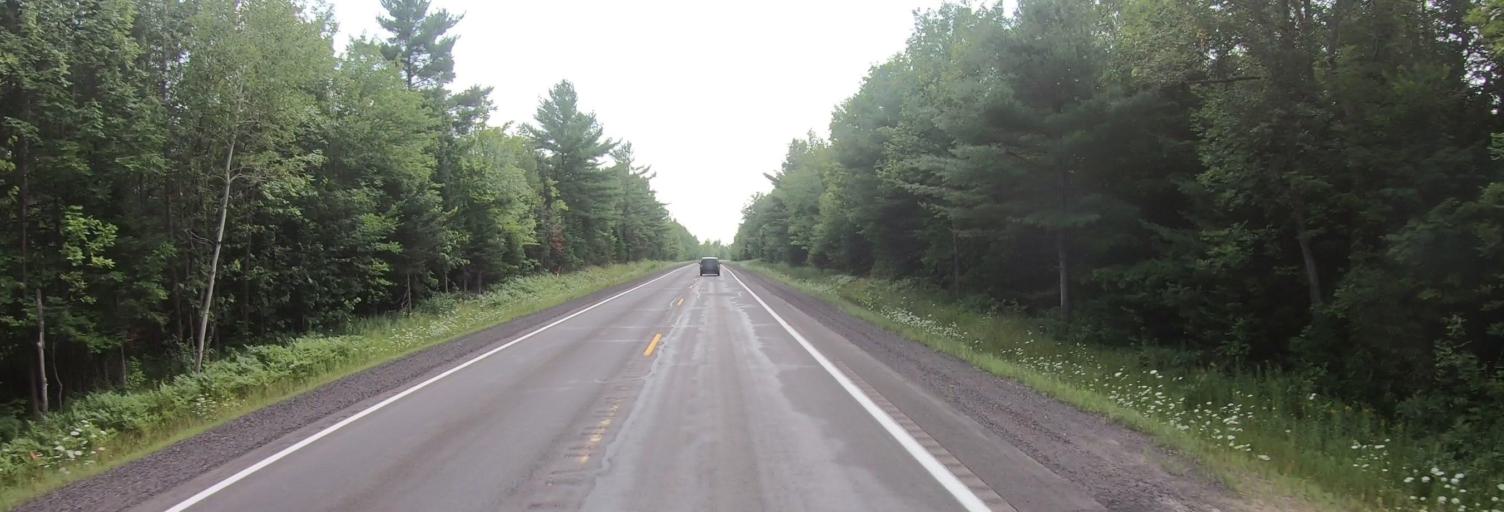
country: US
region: Michigan
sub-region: Ontonagon County
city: Ontonagon
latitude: 46.7405
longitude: -89.1085
